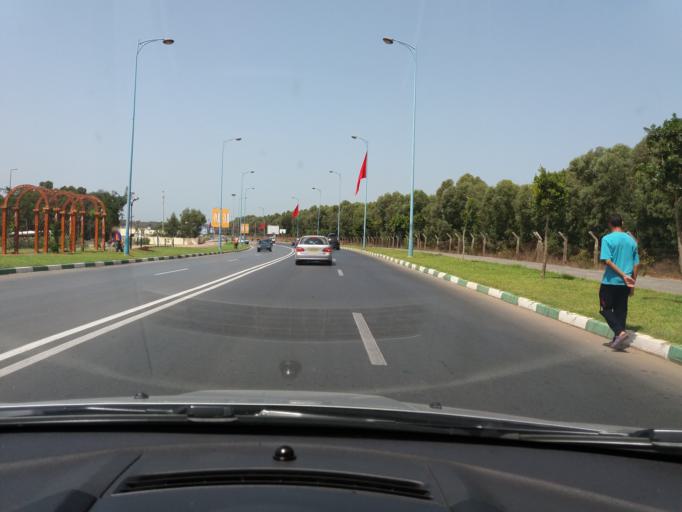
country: MA
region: Gharb-Chrarda-Beni Hssen
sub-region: Kenitra Province
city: Kenitra
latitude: 34.2718
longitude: -6.6312
